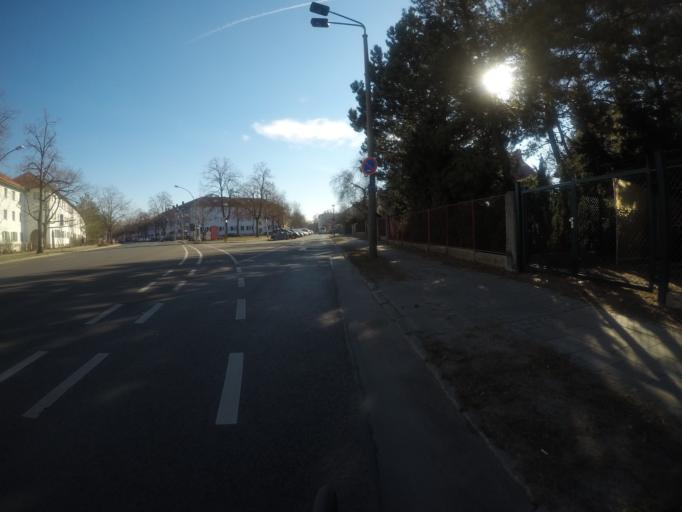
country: DE
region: Berlin
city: Kopenick Bezirk
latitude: 52.4675
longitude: 13.5739
